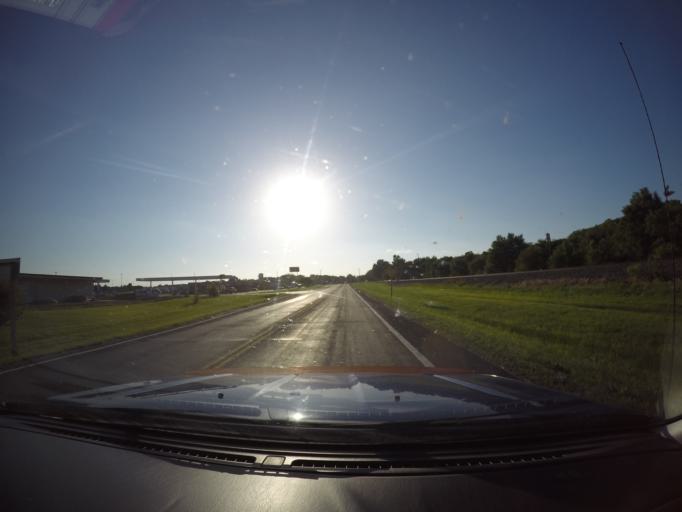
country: US
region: Kansas
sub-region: Pottawatomie County
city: Saint Marys
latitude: 39.1885
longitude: -96.0551
